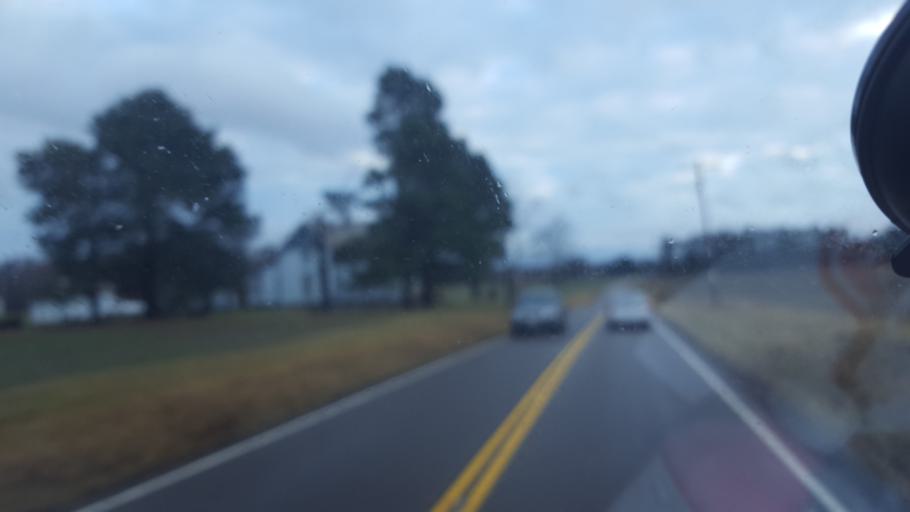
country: US
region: Ohio
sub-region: Knox County
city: Fredericktown
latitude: 40.5478
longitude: -82.5610
